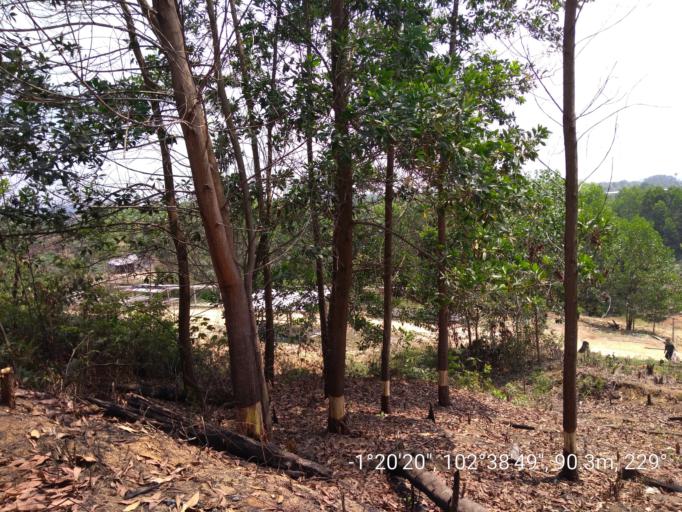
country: ID
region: Jambi
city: Sungaibengkal
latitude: -1.3391
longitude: 102.6472
